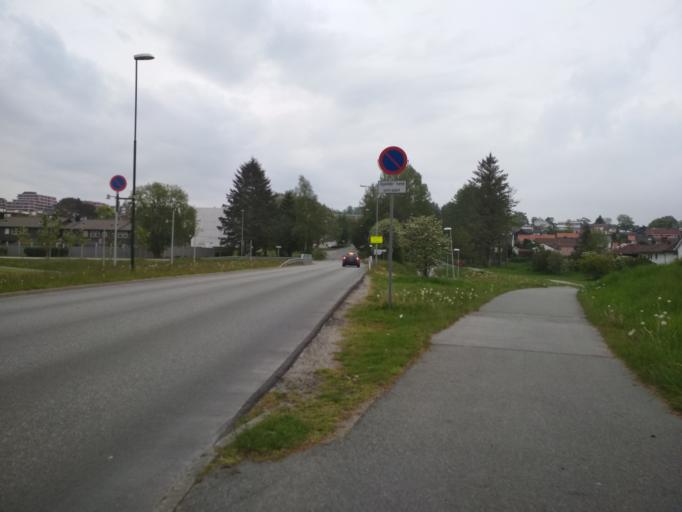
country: NO
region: Rogaland
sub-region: Stavanger
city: Stavanger
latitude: 58.9531
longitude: 5.6873
